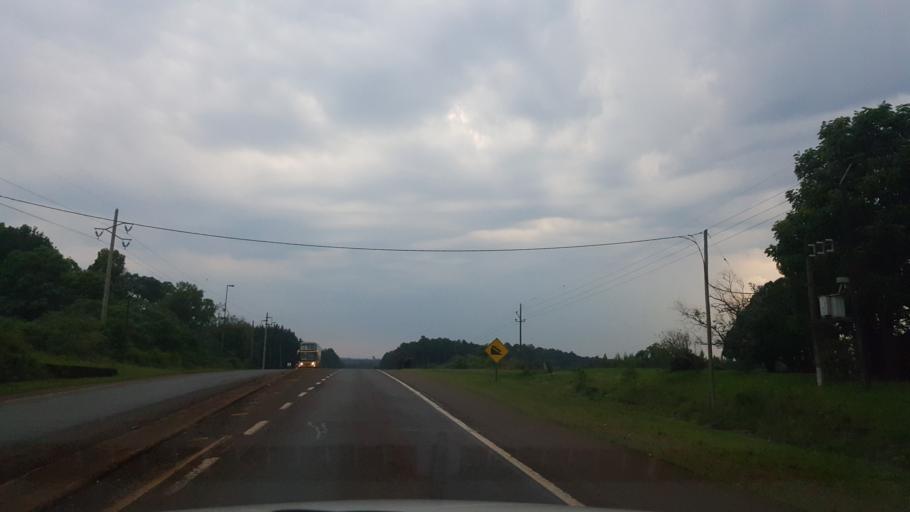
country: AR
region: Misiones
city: Jardin America
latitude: -27.0156
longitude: -55.1920
